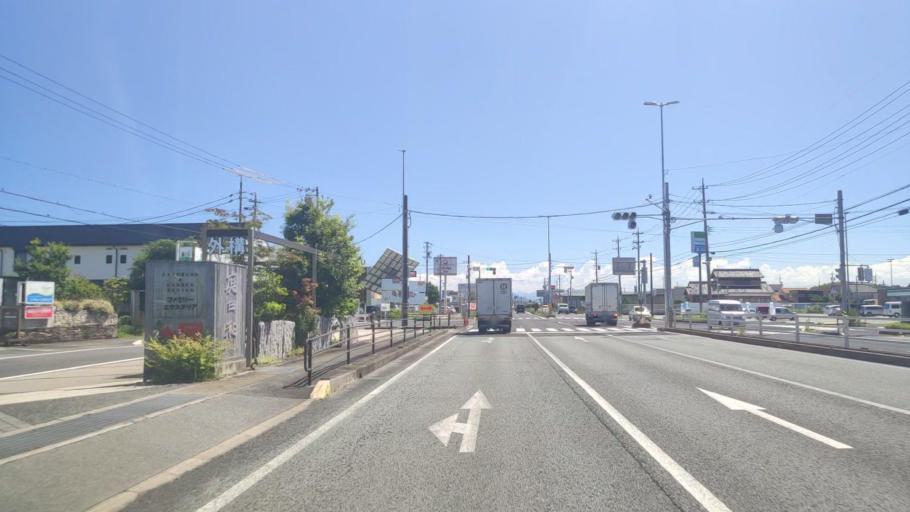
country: JP
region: Mie
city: Kawage
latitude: 34.7768
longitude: 136.5308
